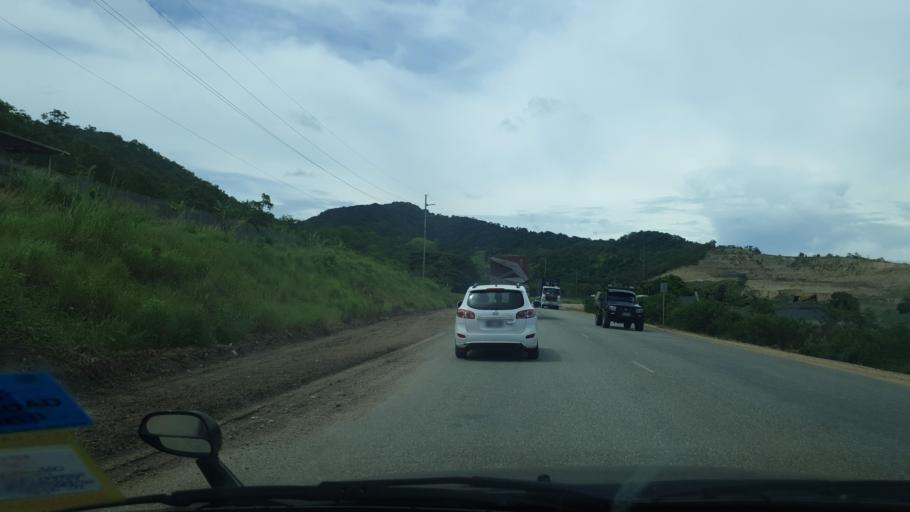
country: PG
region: National Capital
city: Port Moresby
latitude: -9.4190
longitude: 147.0996
